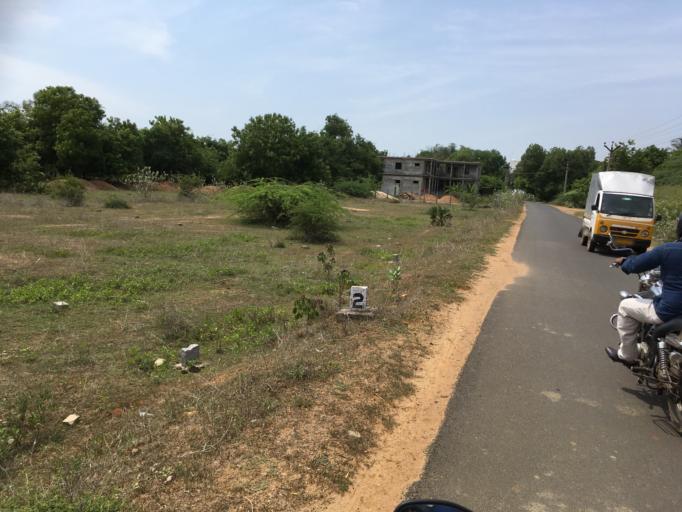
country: IN
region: Tamil Nadu
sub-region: Villupuram
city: Auroville
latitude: 12.0075
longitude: 79.7964
